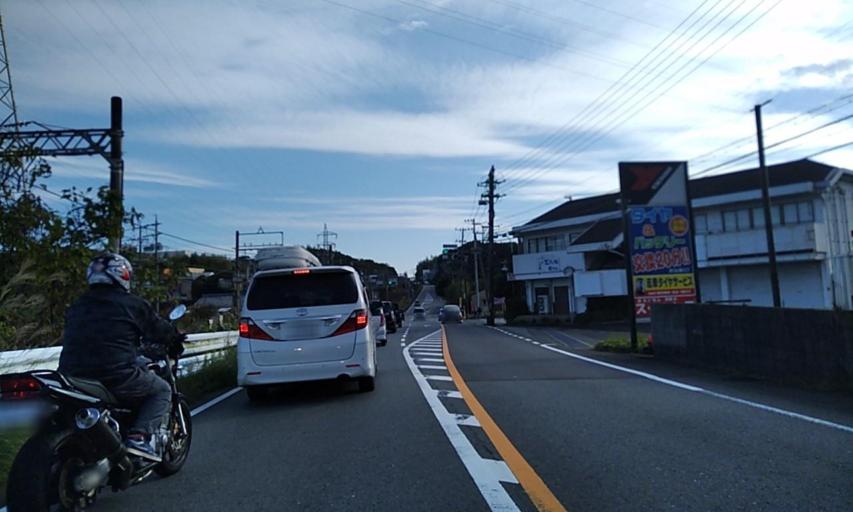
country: JP
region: Mie
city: Toba
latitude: 34.3389
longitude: 136.8171
